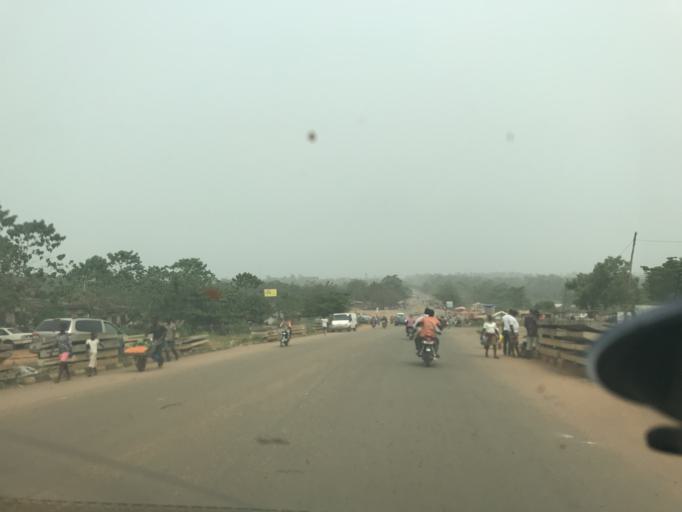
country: NG
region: Ogun
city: Ilaro
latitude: 6.8958
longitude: 3.0214
